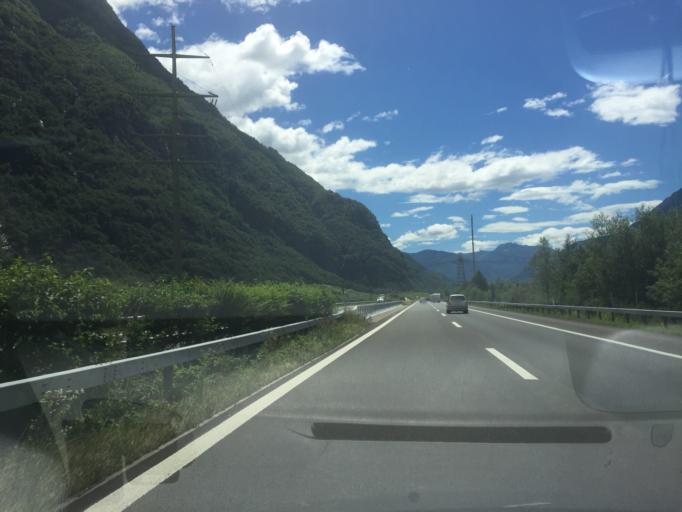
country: CH
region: Ticino
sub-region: Riviera District
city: Biasca
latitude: 46.3355
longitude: 8.9734
